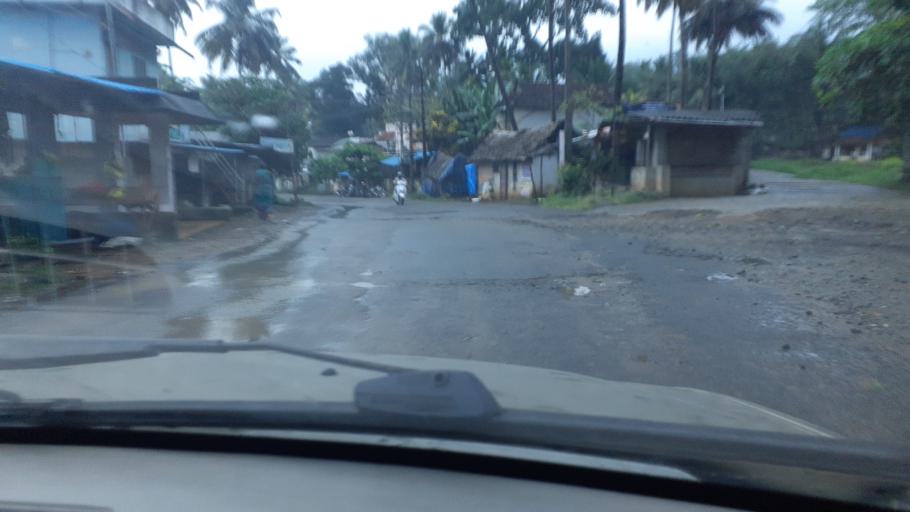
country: IN
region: Tamil Nadu
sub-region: Kanniyakumari
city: Padmanabhapuram
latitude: 8.3628
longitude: 77.3120
